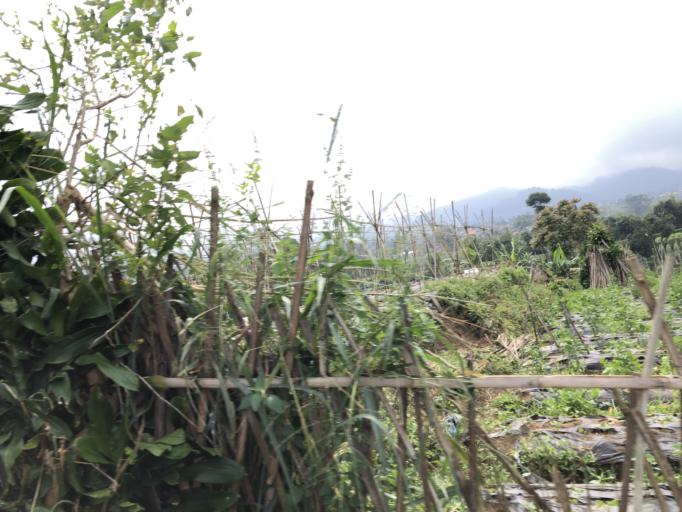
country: ID
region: West Java
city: Lembang
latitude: -6.8153
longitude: 107.6480
